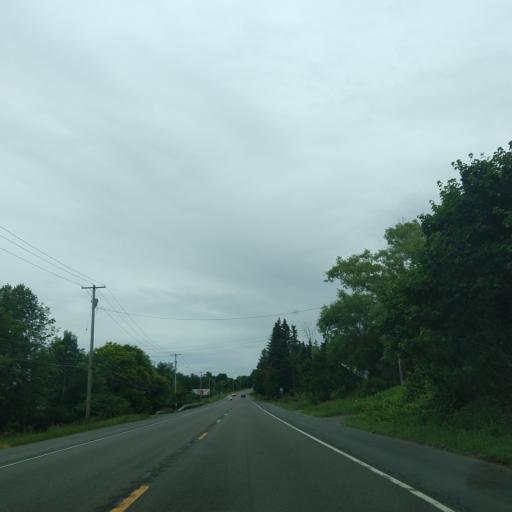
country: US
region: New York
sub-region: Tompkins County
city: Northeast Ithaca
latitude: 42.4783
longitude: -76.3813
